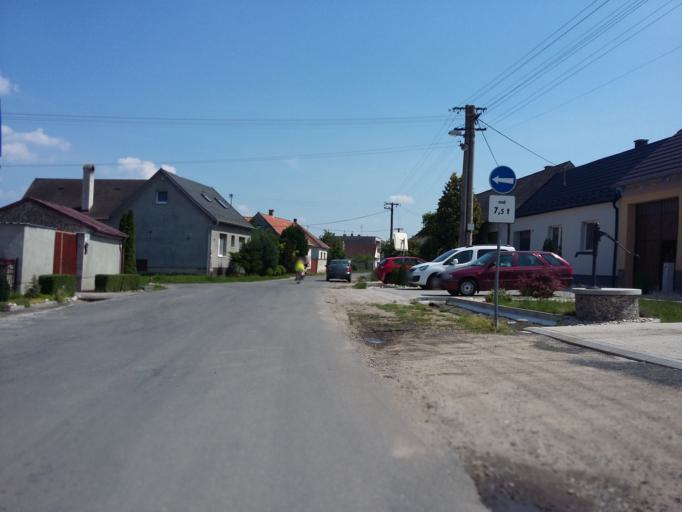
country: AT
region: Lower Austria
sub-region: Politischer Bezirk Ganserndorf
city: Drosing
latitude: 48.5052
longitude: 16.9683
